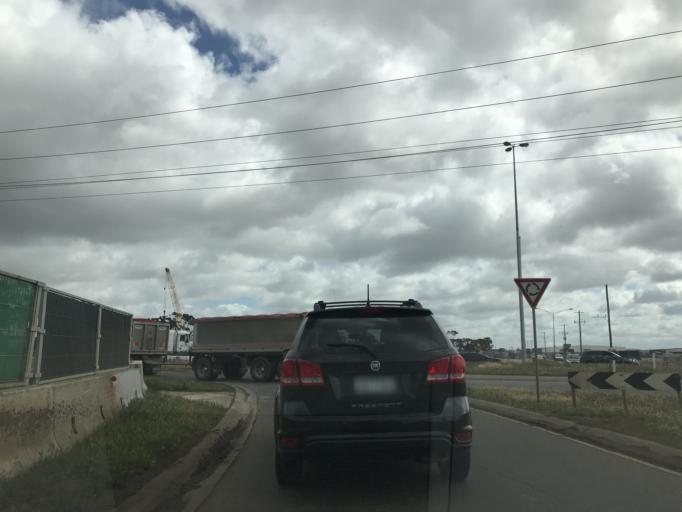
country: AU
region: Victoria
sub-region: Wyndham
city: Truganina
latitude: -37.8253
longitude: 144.7488
